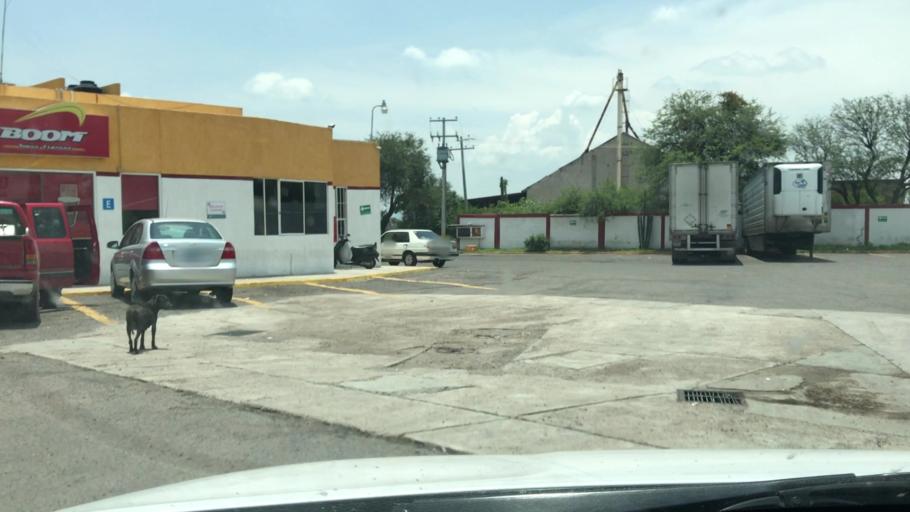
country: MX
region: Guanajuato
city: Penjamo
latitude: 20.4330
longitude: -101.7007
